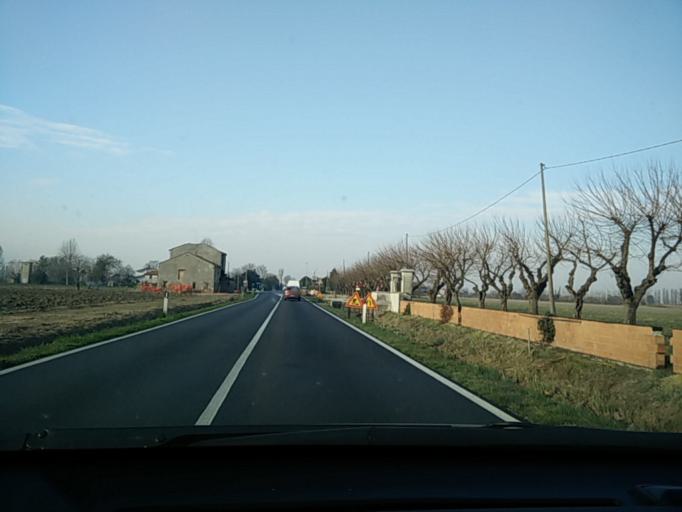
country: IT
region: Veneto
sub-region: Provincia di Treviso
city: San Biagio di Callalta
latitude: 45.6908
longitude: 12.3990
